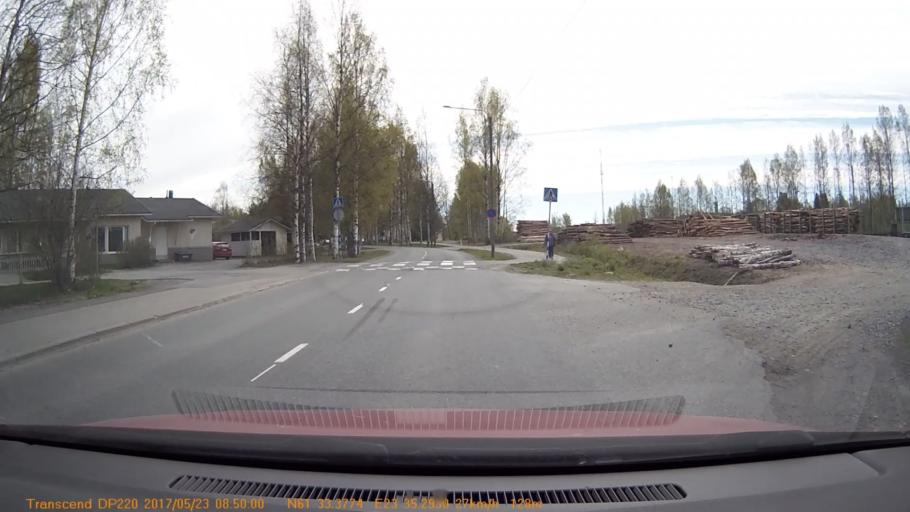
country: FI
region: Pirkanmaa
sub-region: Tampere
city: Yloejaervi
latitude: 61.5564
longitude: 23.5881
